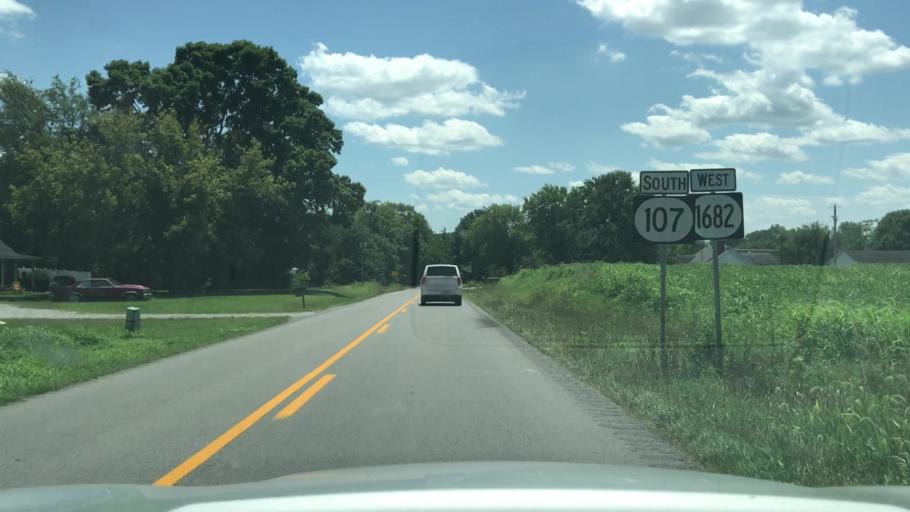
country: US
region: Kentucky
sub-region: Christian County
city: Hopkinsville
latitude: 36.8932
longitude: -87.4527
